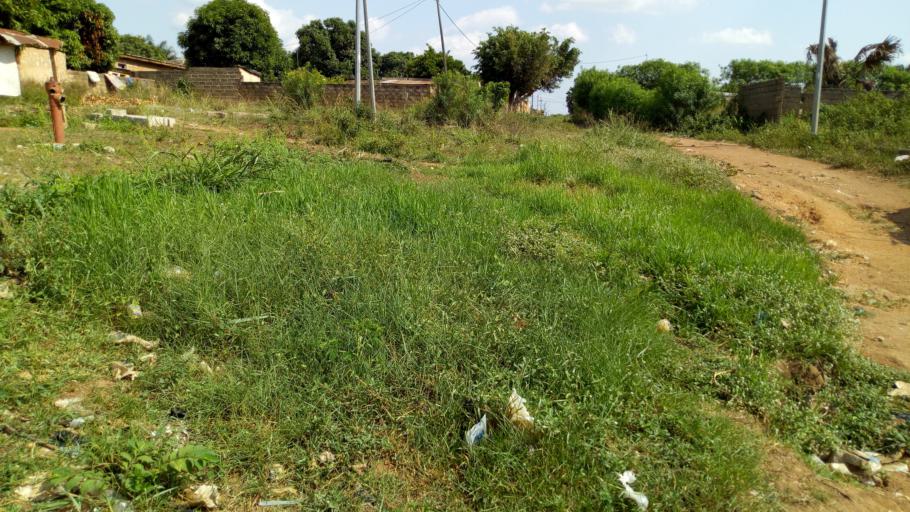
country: CI
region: Vallee du Bandama
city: Bouake
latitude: 7.6718
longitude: -5.0575
